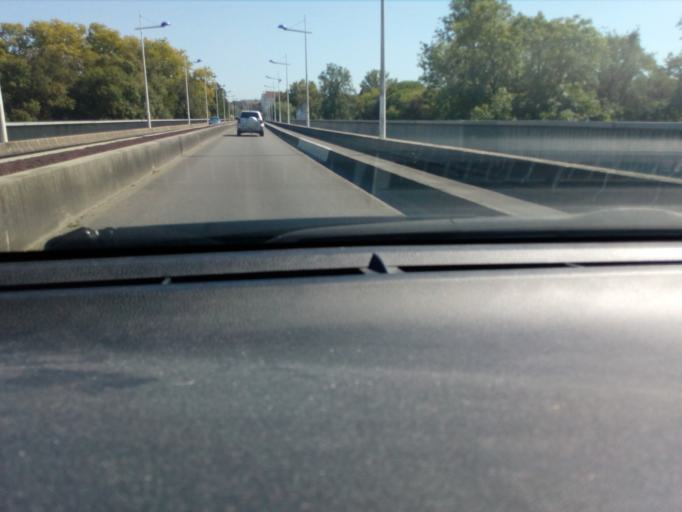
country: FR
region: Poitou-Charentes
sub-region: Departement de la Charente
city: Angouleme
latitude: 45.6624
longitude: 0.1576
